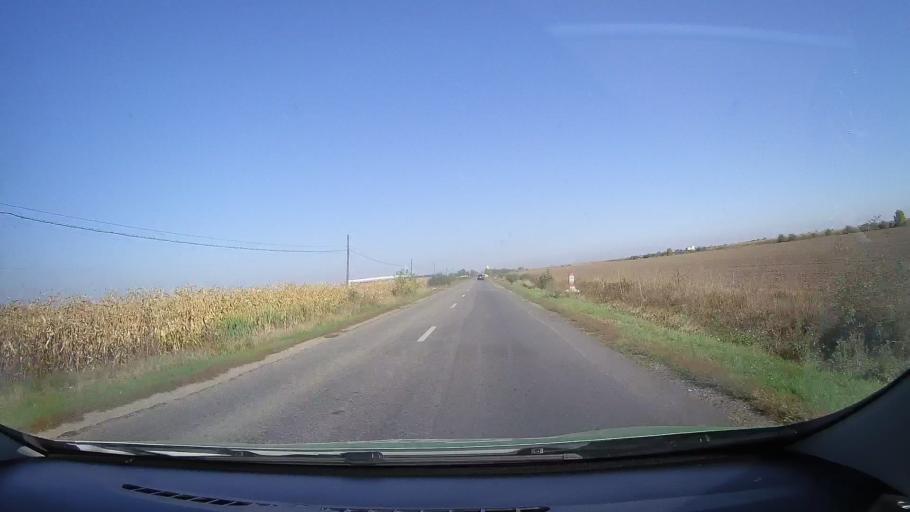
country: RO
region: Satu Mare
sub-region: Oras Tasnad
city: Tasnad
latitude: 47.5010
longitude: 22.5745
